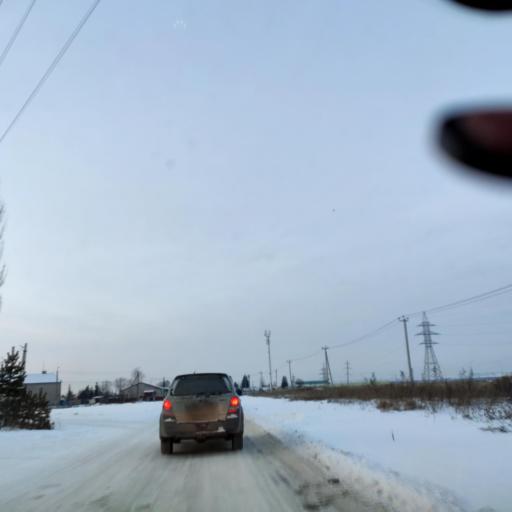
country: RU
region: Bashkortostan
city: Mikhaylovka
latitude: 54.8675
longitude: 55.7409
